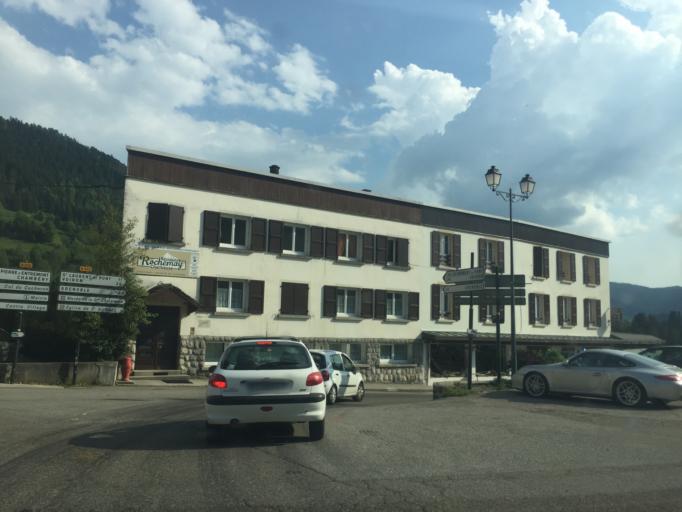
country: FR
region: Rhone-Alpes
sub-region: Departement de l'Isere
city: Saint-Hilaire
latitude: 45.3422
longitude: 5.8140
